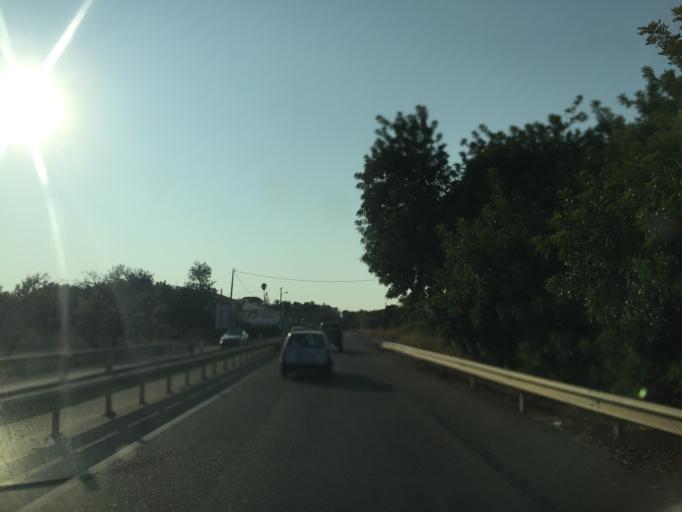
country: PT
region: Faro
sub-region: Faro
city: Santa Barbara de Nexe
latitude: 37.0743
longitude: -7.9807
